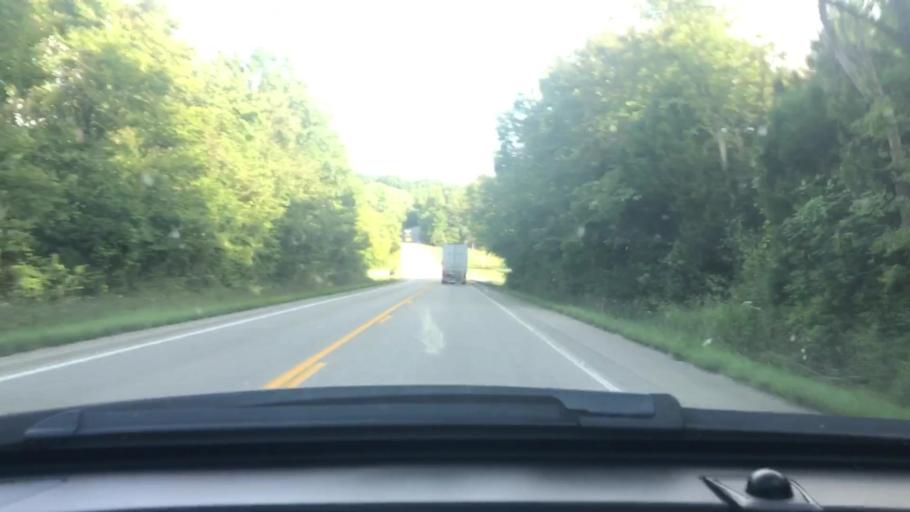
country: US
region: Arkansas
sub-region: Randolph County
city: Pocahontas
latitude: 36.2189
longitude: -91.2205
